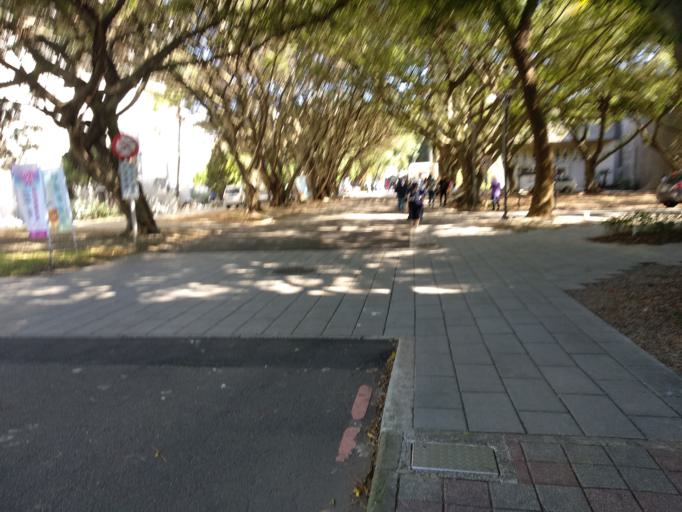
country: TW
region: Taiwan
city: Taoyuan City
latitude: 24.9563
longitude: 121.2428
